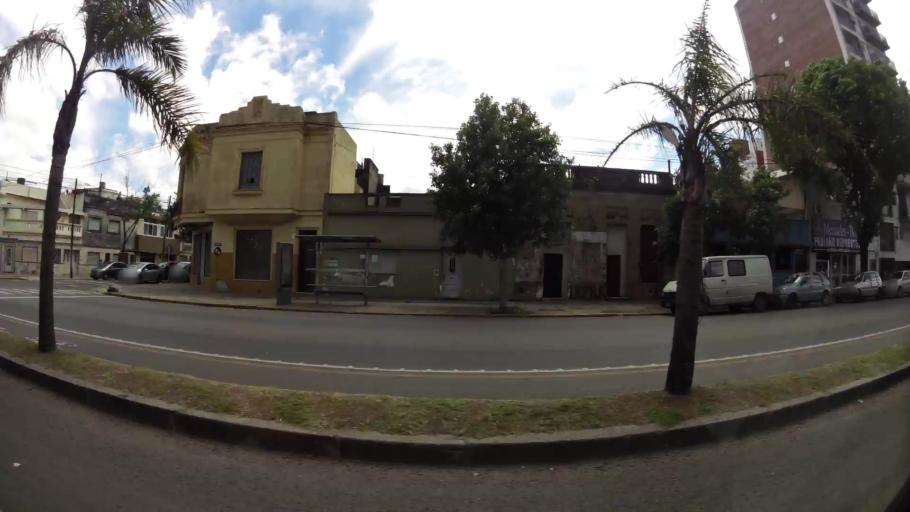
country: AR
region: Santa Fe
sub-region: Departamento de Rosario
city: Rosario
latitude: -32.9667
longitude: -60.6486
